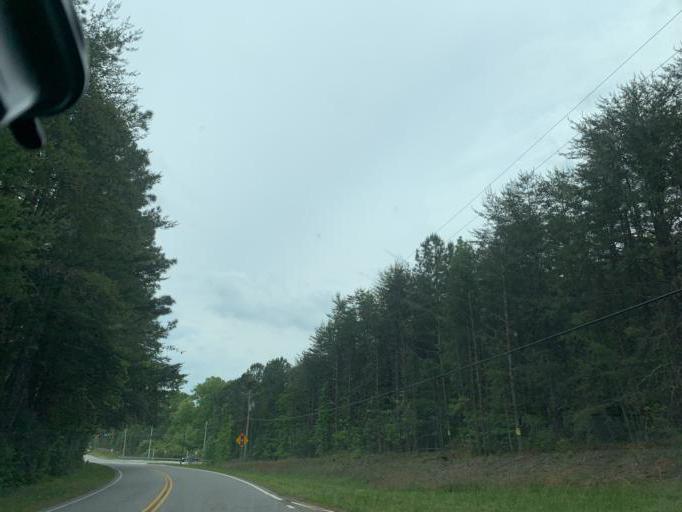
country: US
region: Georgia
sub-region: Forsyth County
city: Cumming
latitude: 34.2071
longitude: -84.1192
